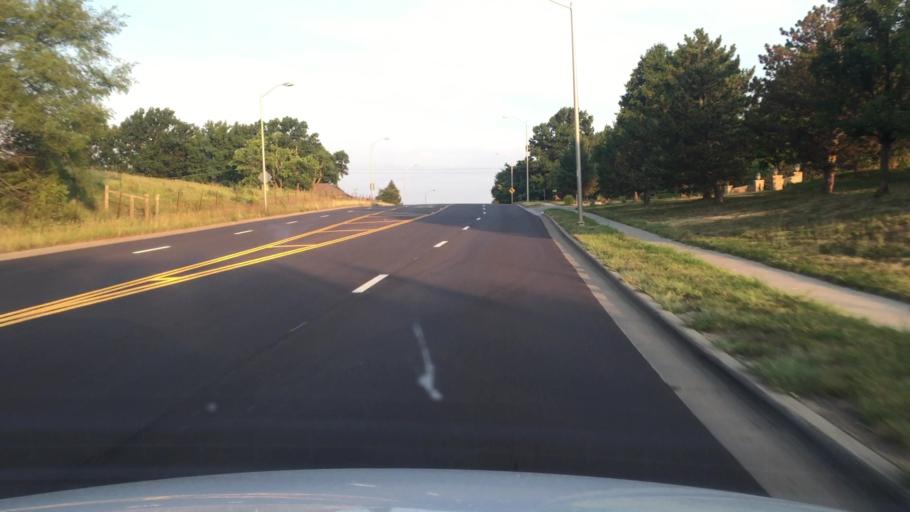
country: US
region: Kansas
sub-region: Johnson County
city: Shawnee
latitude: 39.0226
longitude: -94.7735
